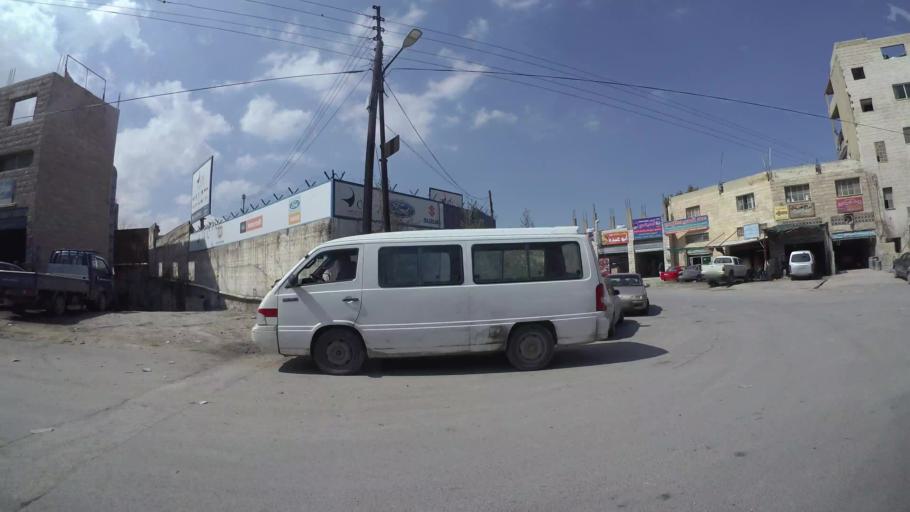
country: JO
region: Zarqa
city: Russeifa
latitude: 31.9916
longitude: 36.0012
